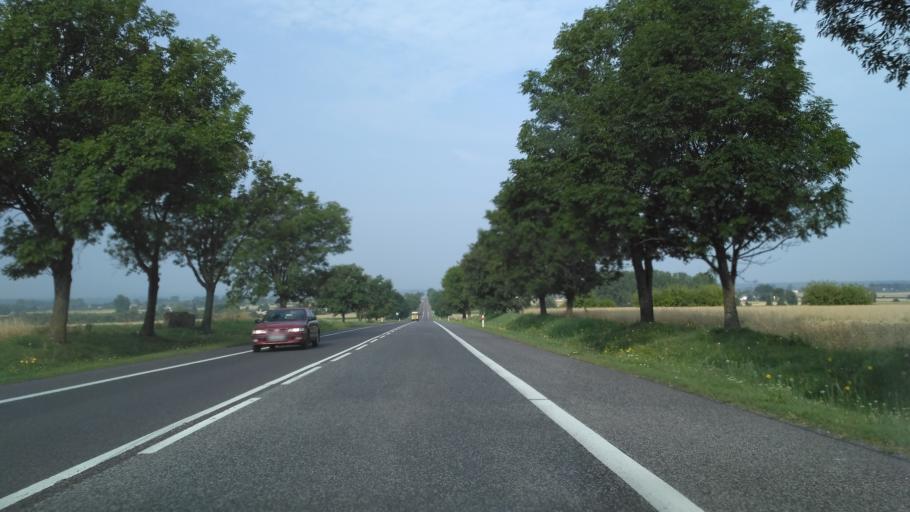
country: PL
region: Lublin Voivodeship
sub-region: Powiat swidnicki
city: Trawniki
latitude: 51.1691
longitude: 23.0973
